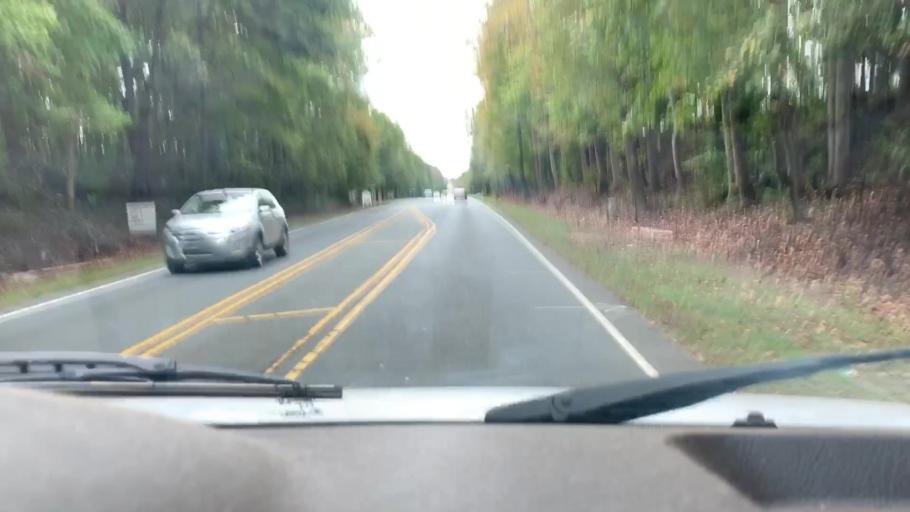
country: US
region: North Carolina
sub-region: Mecklenburg County
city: Cornelius
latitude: 35.4530
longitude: -80.8673
